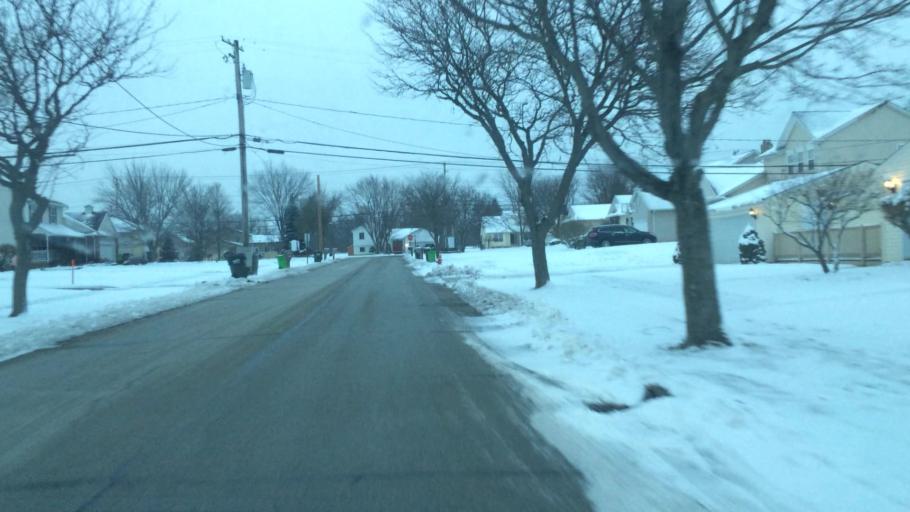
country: US
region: Ohio
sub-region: Cuyahoga County
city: Oakwood
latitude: 41.3739
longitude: -81.5003
